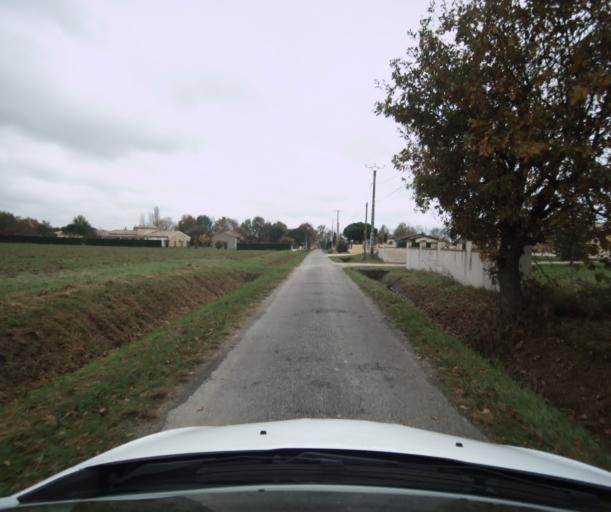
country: FR
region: Midi-Pyrenees
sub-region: Departement du Tarn-et-Garonne
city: Saint-Porquier
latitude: 44.0496
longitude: 1.1726
